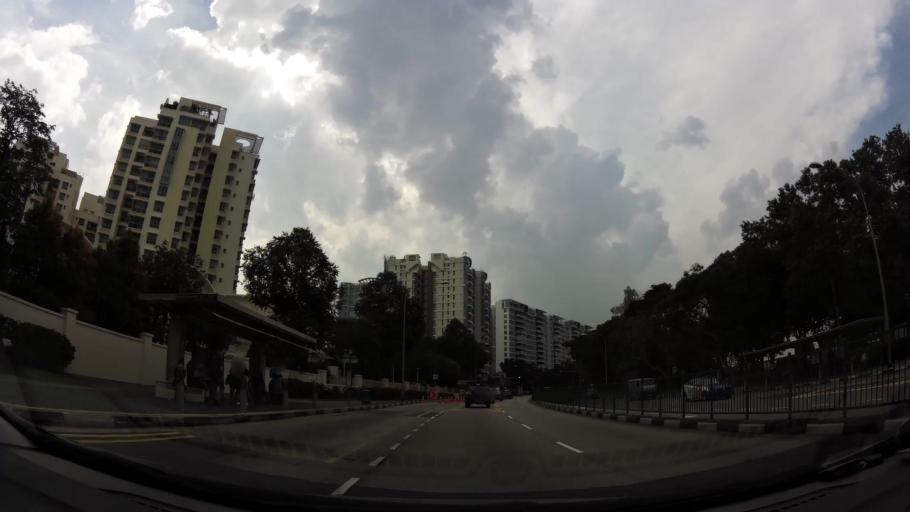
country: SG
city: Singapore
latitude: 1.3382
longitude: 103.9340
